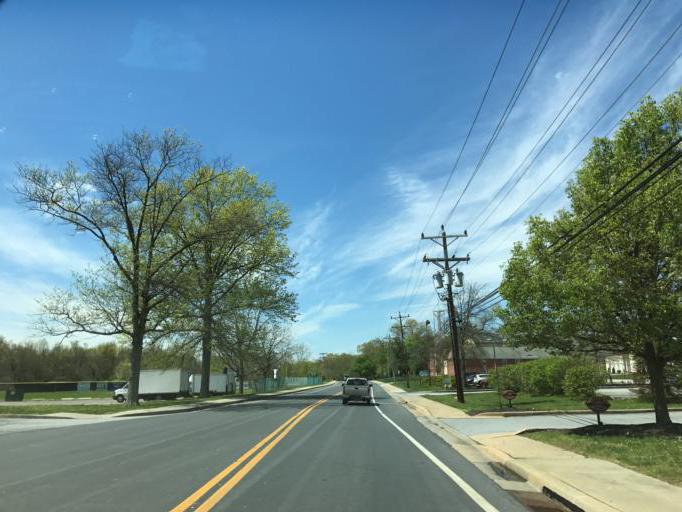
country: US
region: Delaware
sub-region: New Castle County
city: Greenville
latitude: 39.8067
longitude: -75.5497
